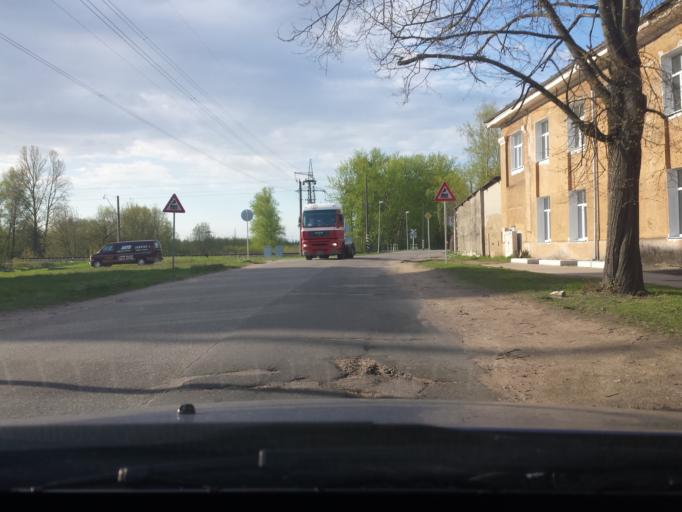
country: LV
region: Riga
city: Jaunciems
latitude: 56.9858
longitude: 24.2062
